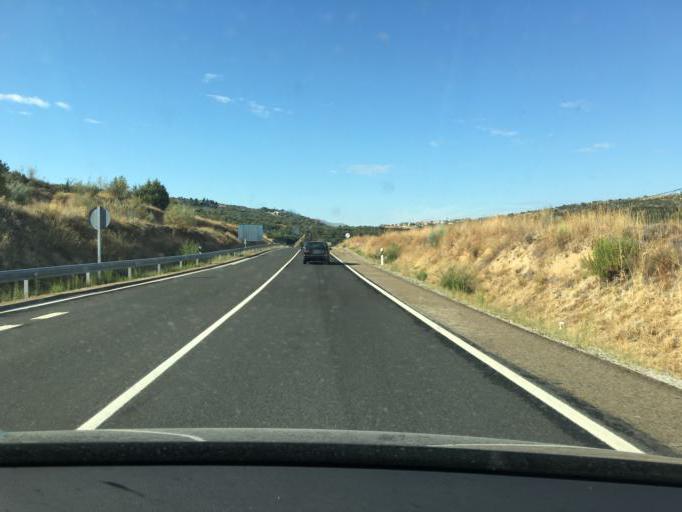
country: ES
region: Madrid
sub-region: Provincia de Madrid
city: Reduena
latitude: 40.8113
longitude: -3.5946
